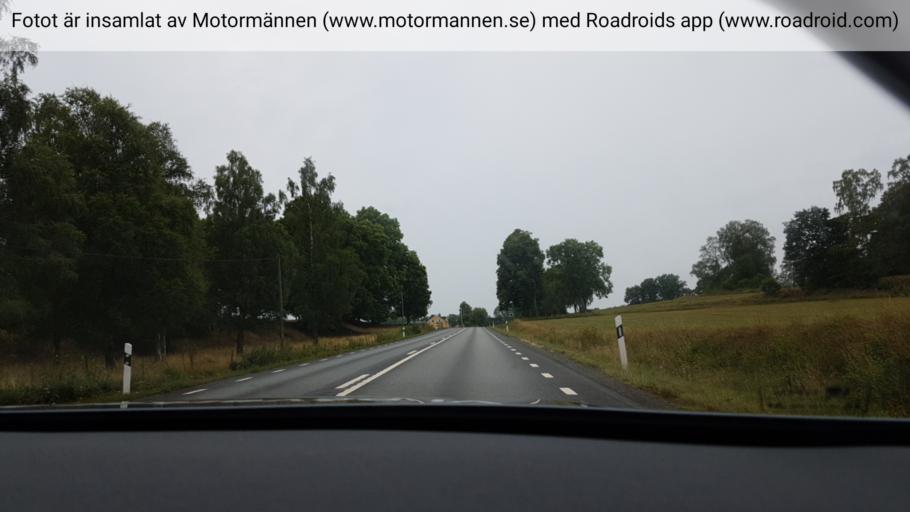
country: SE
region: Joenkoeping
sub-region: Varnamo Kommun
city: Varnamo
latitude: 57.2093
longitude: 14.1033
